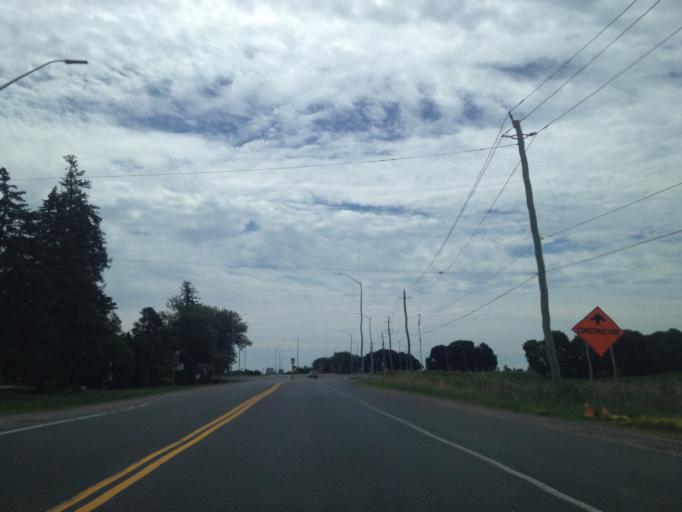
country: CA
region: Ontario
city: Ingersoll
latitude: 43.0302
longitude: -80.8577
